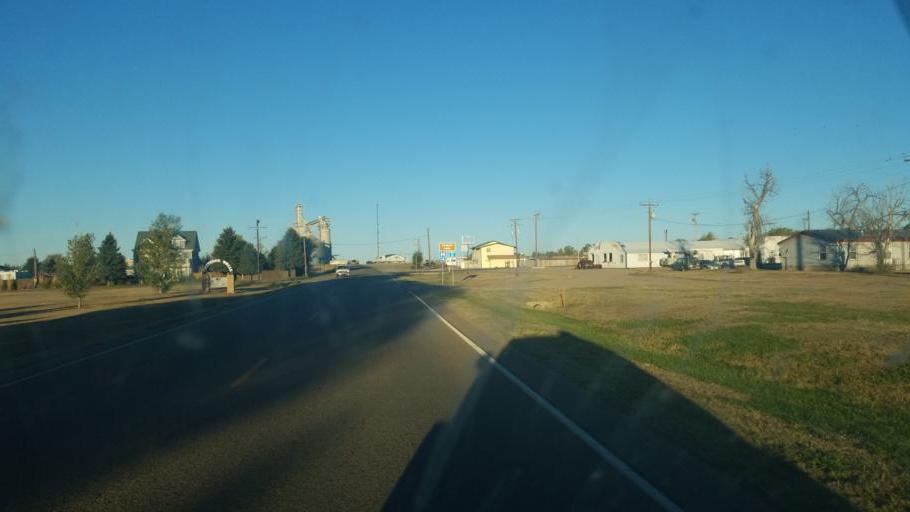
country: US
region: Colorado
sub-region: Cheyenne County
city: Cheyenne Wells
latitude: 38.8165
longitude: -102.3540
